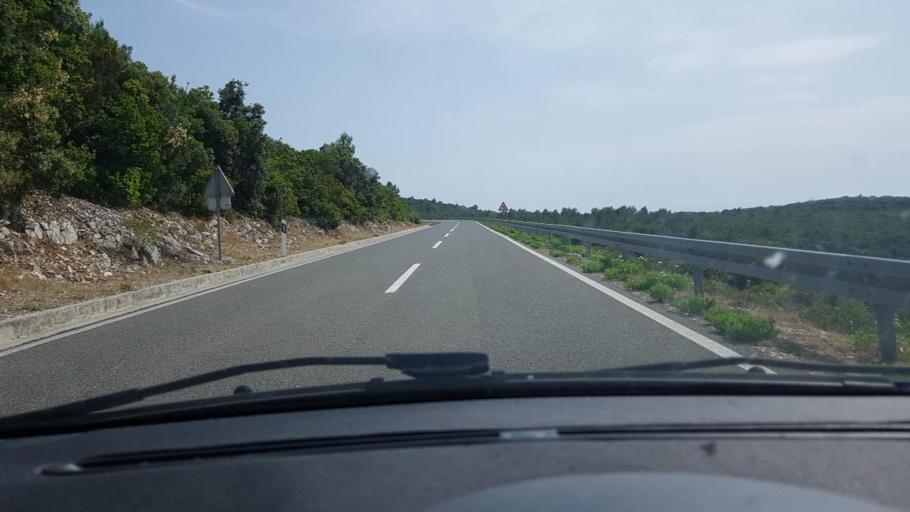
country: HR
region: Dubrovacko-Neretvanska
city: Smokvica
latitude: 42.9527
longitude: 16.9423
